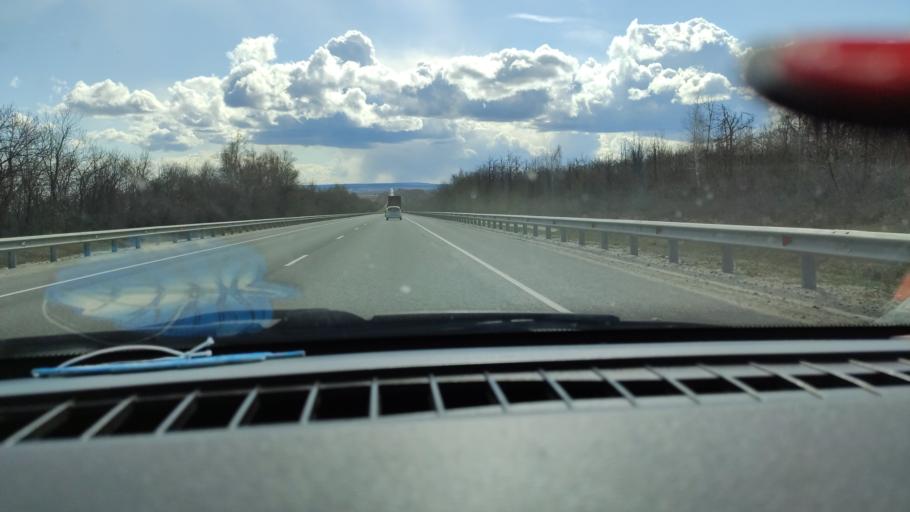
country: RU
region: Saratov
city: Khvalynsk
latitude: 52.6168
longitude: 48.1669
